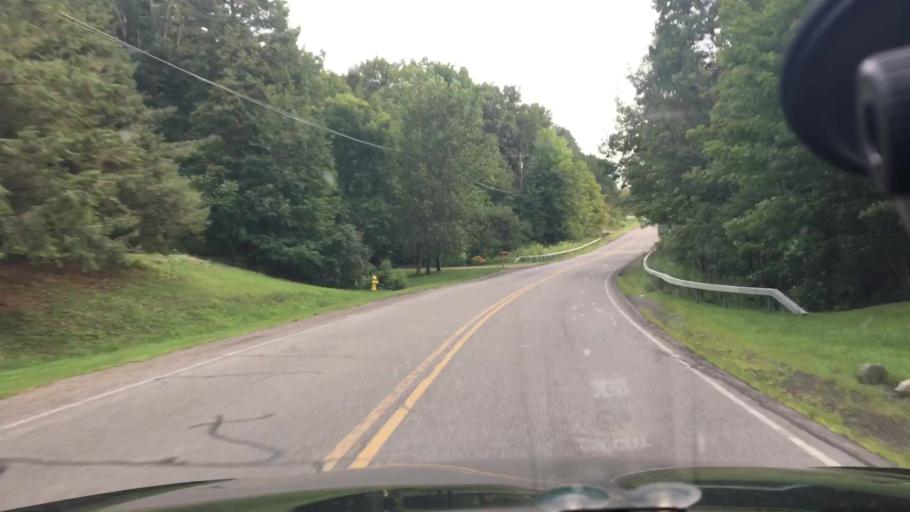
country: US
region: New York
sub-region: Erie County
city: Orchard Park
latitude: 42.7275
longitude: -78.7322
